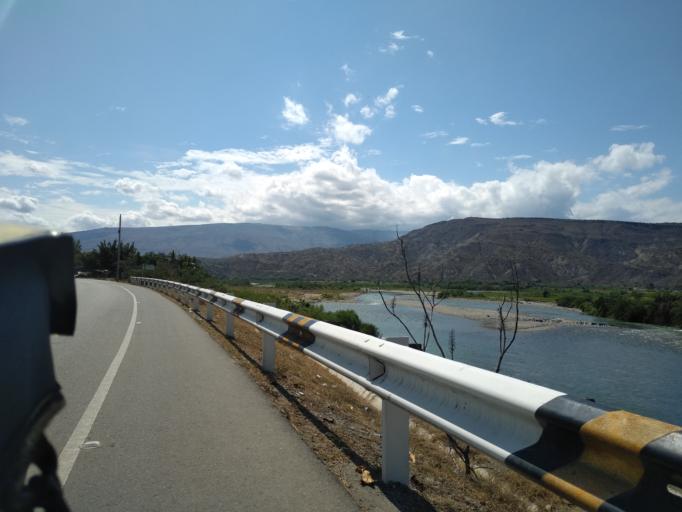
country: PE
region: Cajamarca
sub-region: Provincia de Cutervo
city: Choros
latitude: -5.8387
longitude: -78.7554
